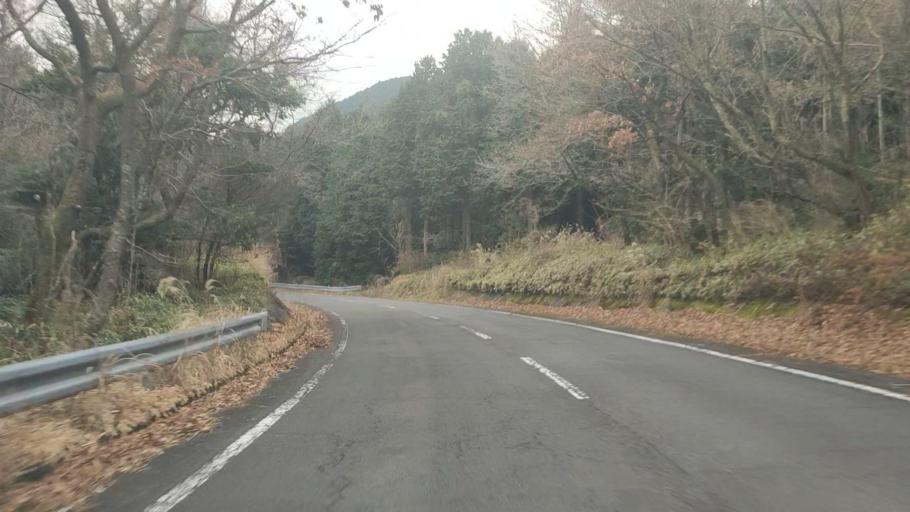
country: JP
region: Nagasaki
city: Shimabara
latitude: 32.7928
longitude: 130.2813
